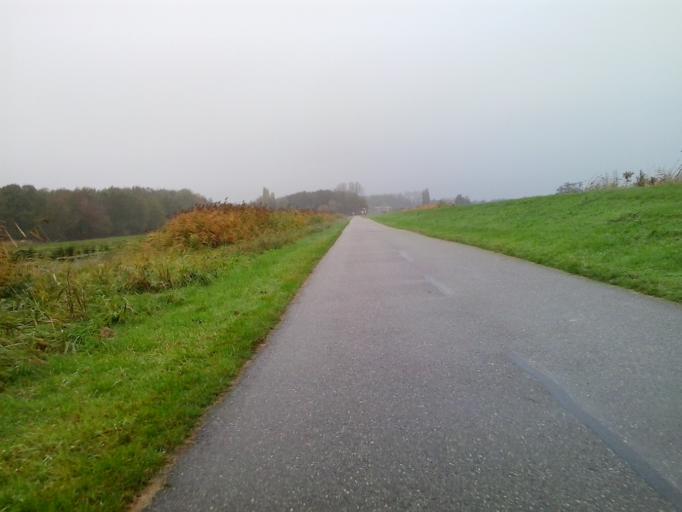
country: NL
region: South Holland
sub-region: Gemeente Lansingerland
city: Bleiswijk
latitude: 51.9854
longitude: 4.5476
